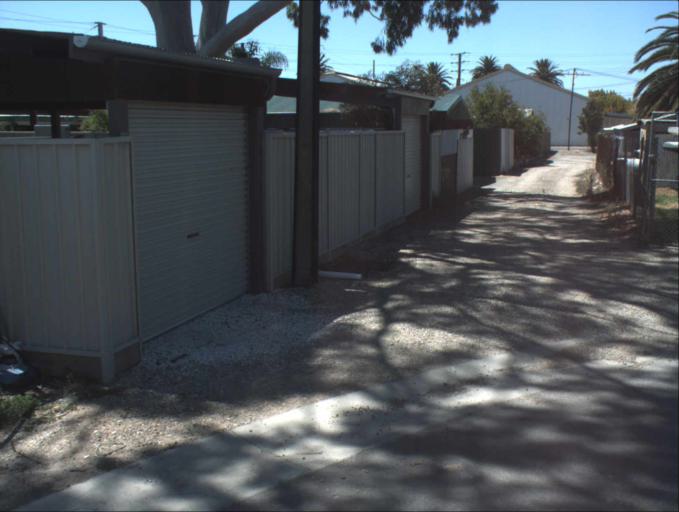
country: AU
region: South Australia
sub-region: Port Adelaide Enfield
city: Alberton
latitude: -34.8539
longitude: 138.5077
